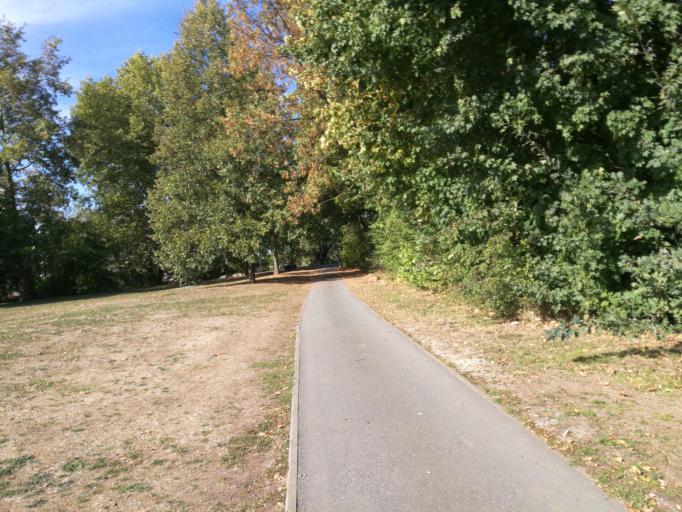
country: DE
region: Bavaria
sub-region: Regierungsbezirk Mittelfranken
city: Furth
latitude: 49.4856
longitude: 10.9875
